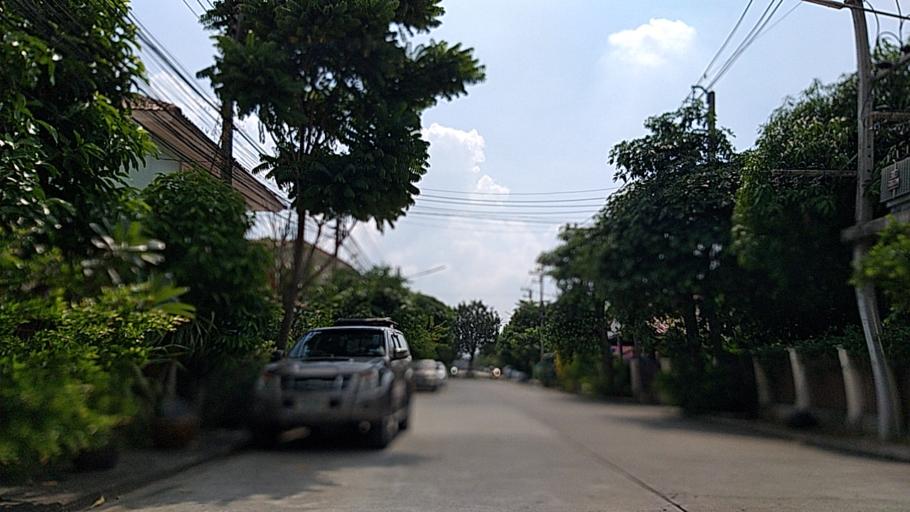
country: TH
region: Pathum Thani
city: Ban Rangsit
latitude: 14.0417
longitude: 100.7653
